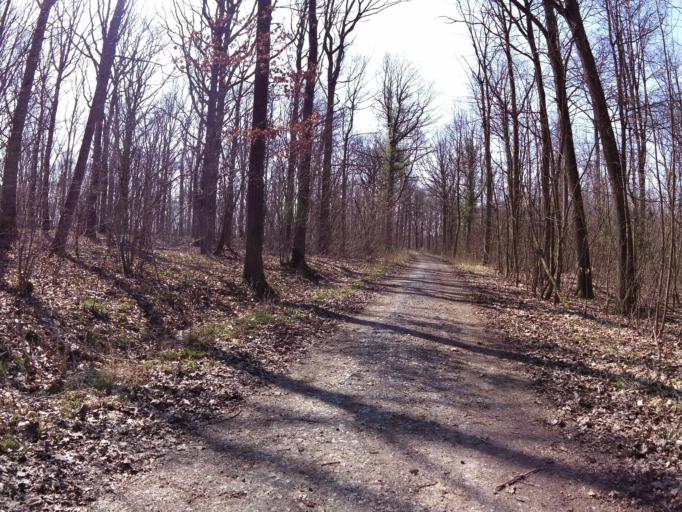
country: DE
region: Bavaria
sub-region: Regierungsbezirk Unterfranken
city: Rottendorf
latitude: 49.8092
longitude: 10.0203
